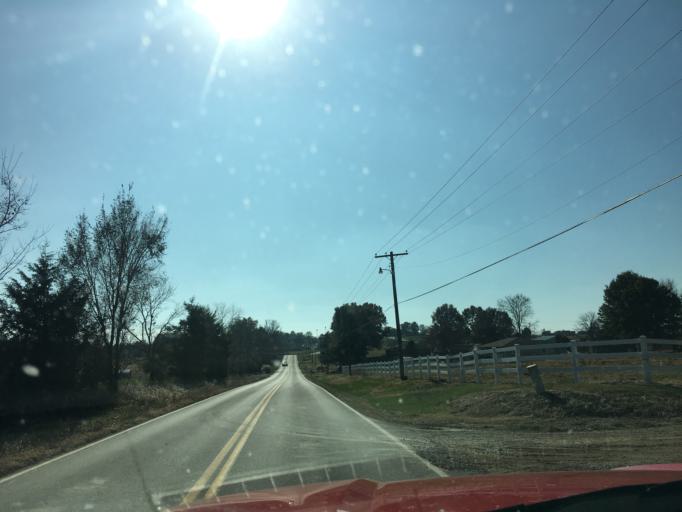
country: US
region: Missouri
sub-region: Cole County
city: Wardsville
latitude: 38.5035
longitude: -92.1759
